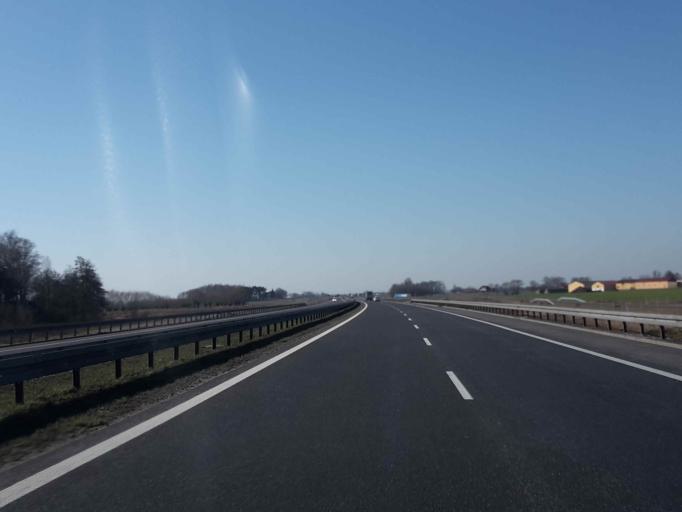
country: PL
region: Greater Poland Voivodeship
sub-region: Powiat poznanski
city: Kleszczewo
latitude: 52.3533
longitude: 17.1845
